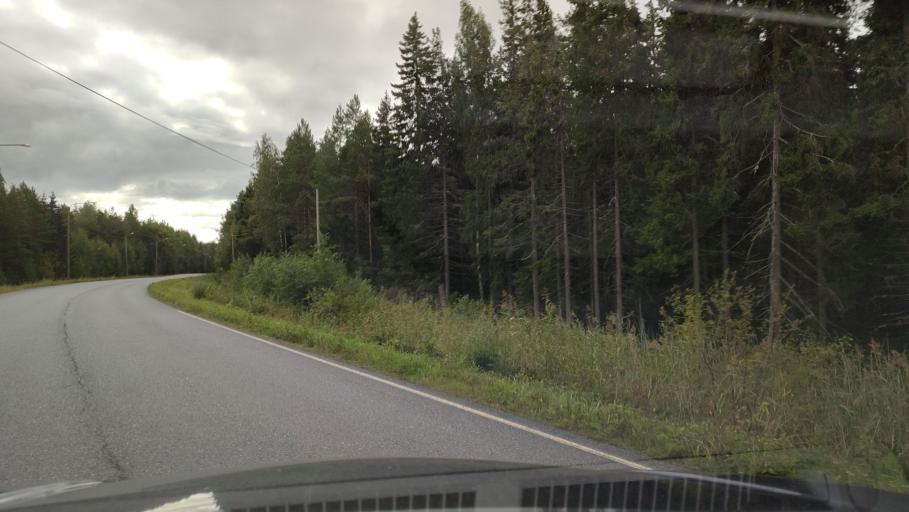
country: FI
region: Ostrobothnia
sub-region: Sydosterbotten
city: Kristinestad
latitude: 62.2626
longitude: 21.3491
